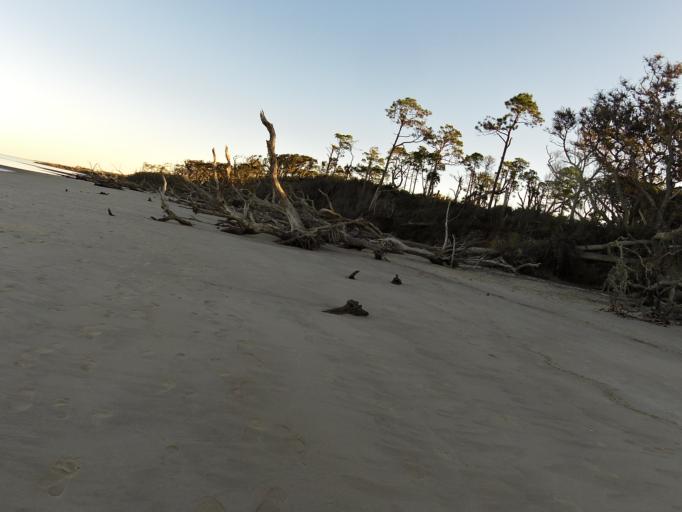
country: US
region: Florida
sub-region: Nassau County
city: Fernandina Beach
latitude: 30.5047
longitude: -81.4515
